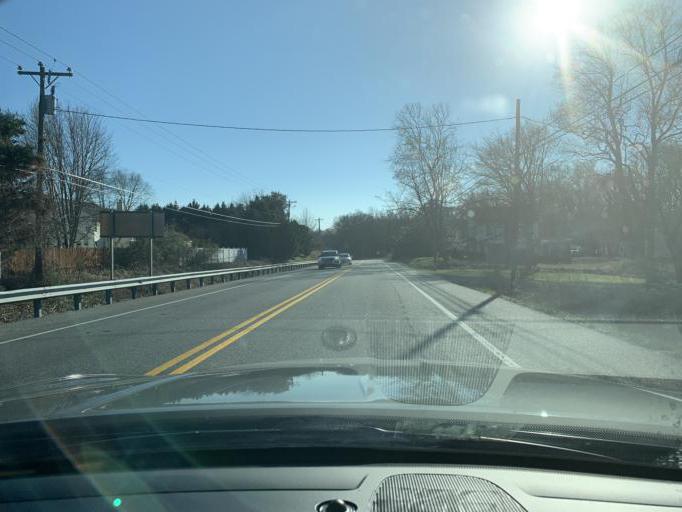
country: US
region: Maryland
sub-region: Queen Anne's County
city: Centreville
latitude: 39.0582
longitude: -76.0534
